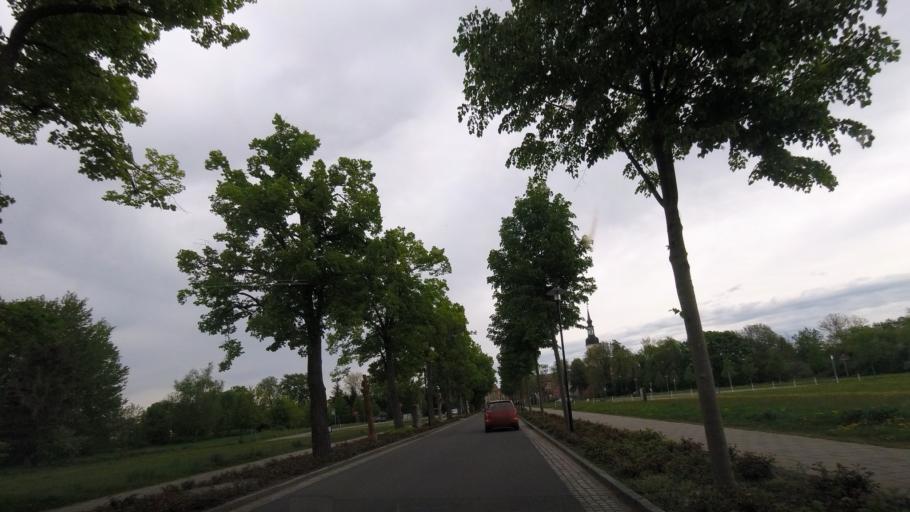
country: DE
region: Brandenburg
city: Lubbenau
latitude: 51.8662
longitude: 13.9659
